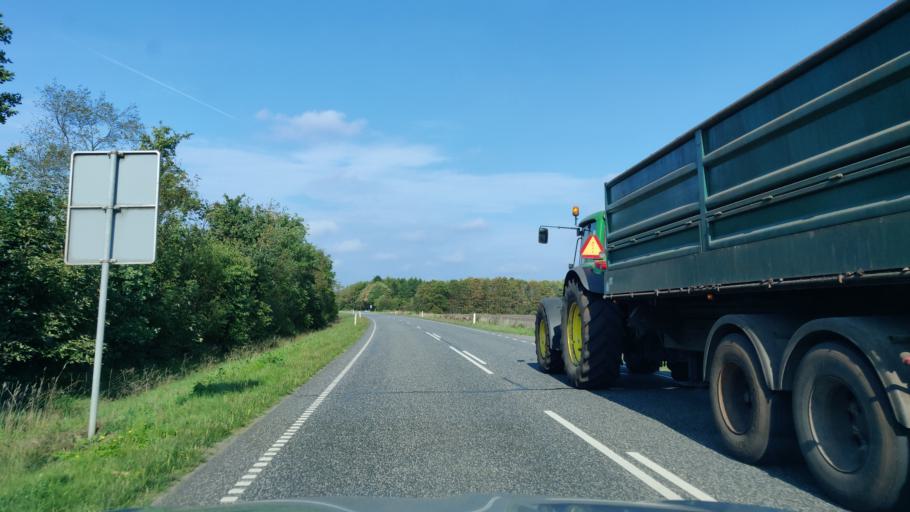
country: DK
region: Central Jutland
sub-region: Herning Kommune
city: Sunds
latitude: 56.2425
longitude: 9.0856
